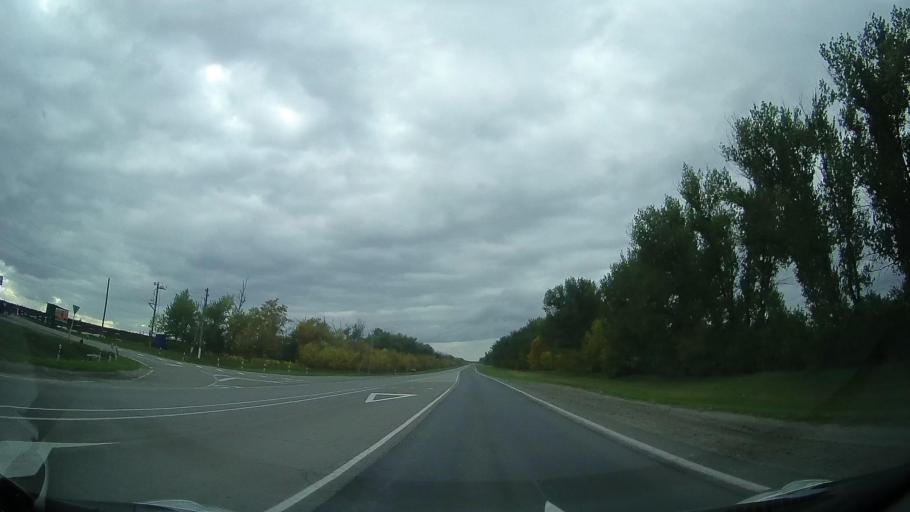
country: RU
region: Rostov
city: Yegorlykskaya
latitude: 46.5489
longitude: 40.7372
